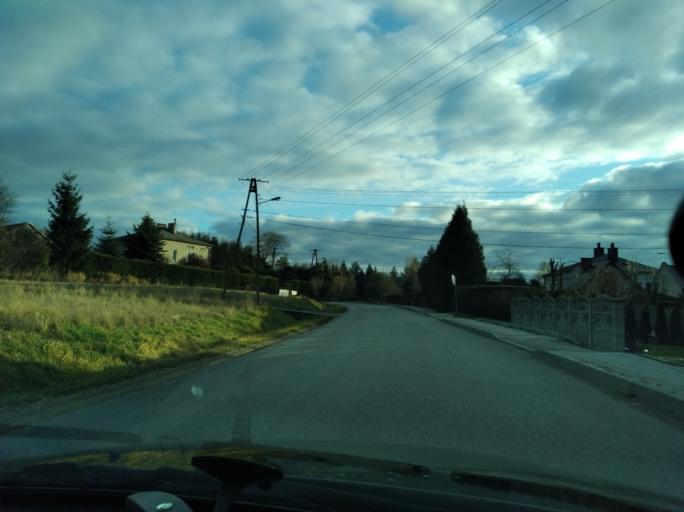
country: PL
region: Subcarpathian Voivodeship
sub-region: Powiat rzeszowski
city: Krasne
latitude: 50.0571
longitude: 22.1199
